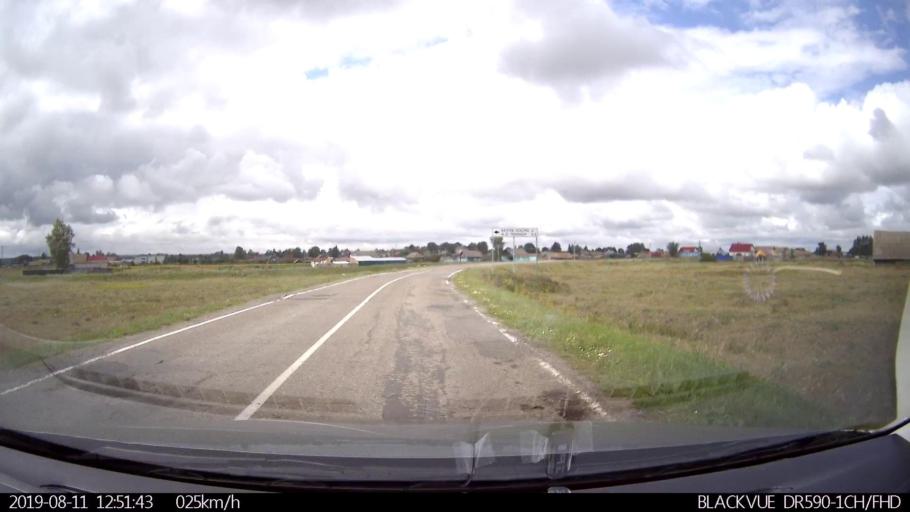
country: RU
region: Ulyanovsk
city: Ignatovka
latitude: 53.8758
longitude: 47.6613
